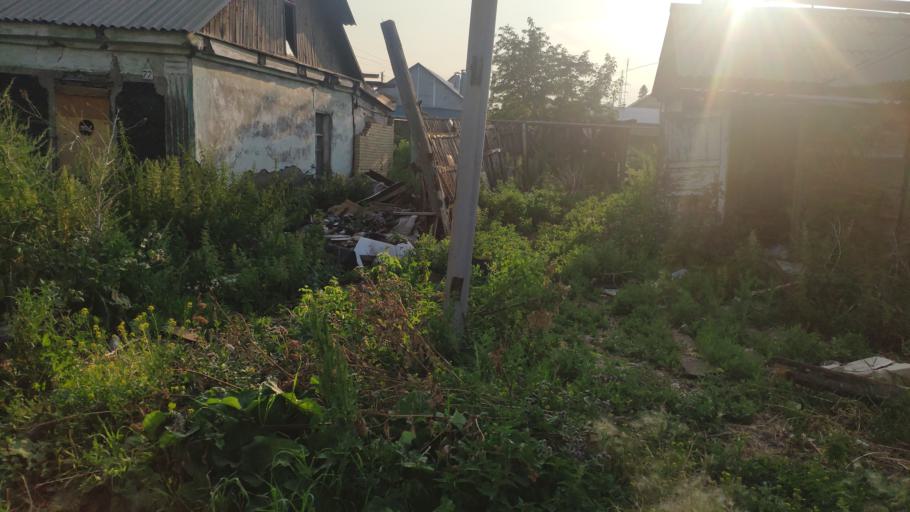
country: RU
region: Chelyabinsk
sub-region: Gorod Magnitogorsk
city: Magnitogorsk
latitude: 53.3733
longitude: 59.0608
